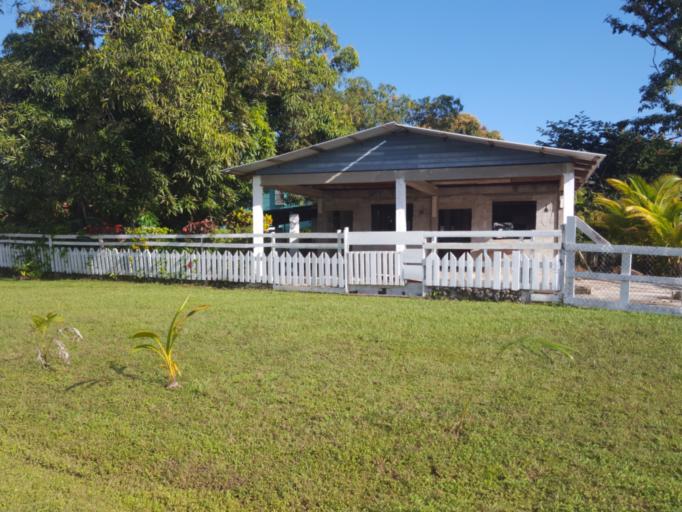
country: BZ
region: Belize
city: Belize City
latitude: 17.5668
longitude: -88.4063
